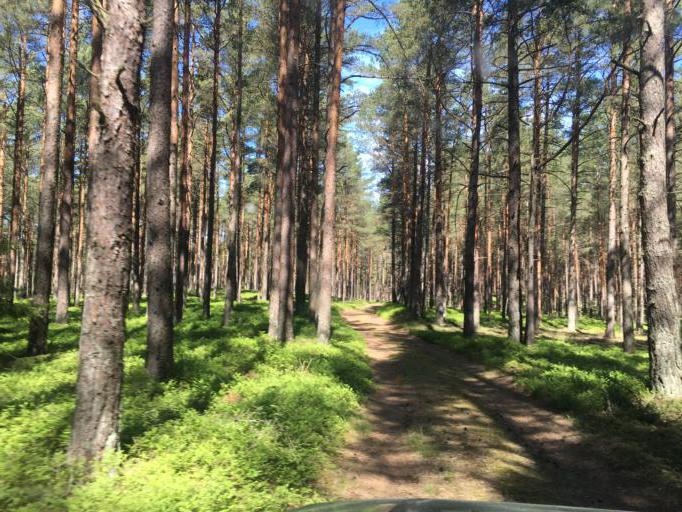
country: LV
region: Ventspils
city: Ventspils
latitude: 57.4726
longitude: 21.6476
